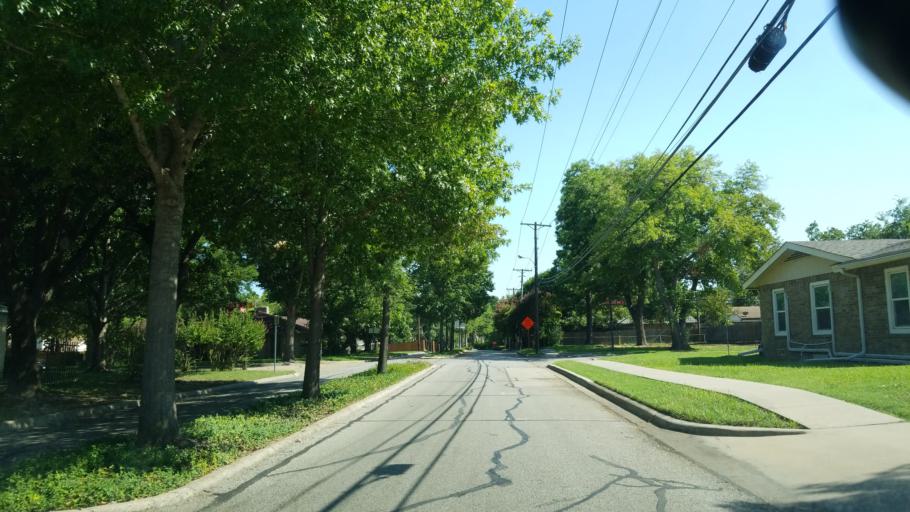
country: US
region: Texas
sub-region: Dallas County
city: Farmers Branch
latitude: 32.9199
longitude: -96.8875
